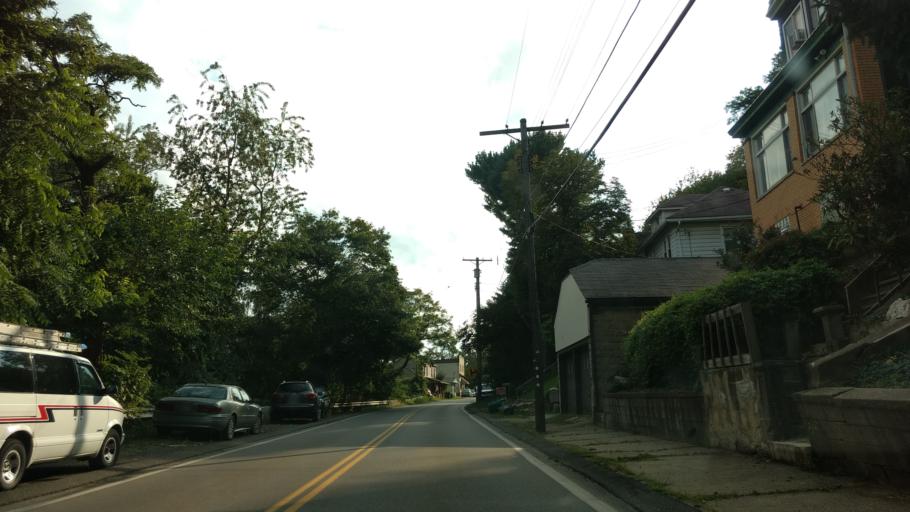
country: US
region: Pennsylvania
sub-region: Allegheny County
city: Bellevue
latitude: 40.4949
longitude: -80.0291
